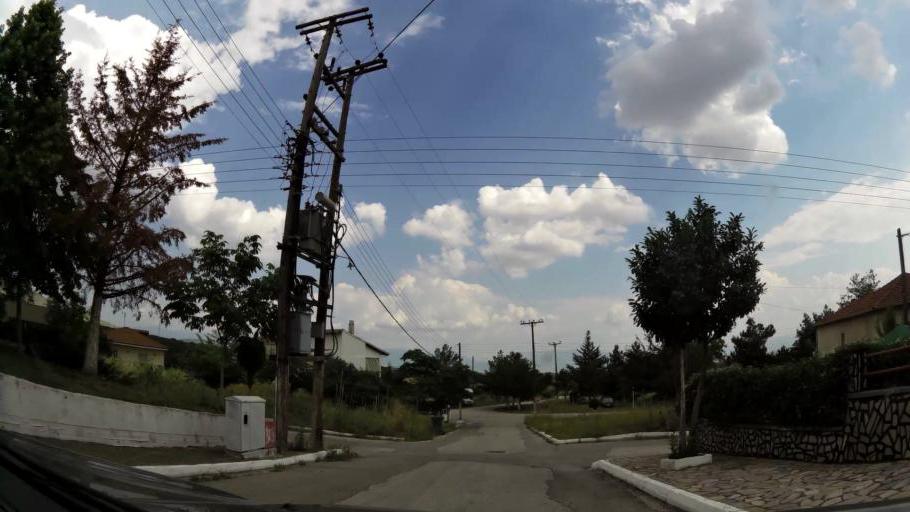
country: GR
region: West Macedonia
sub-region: Nomos Kozanis
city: Koila
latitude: 40.3218
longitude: 21.8251
